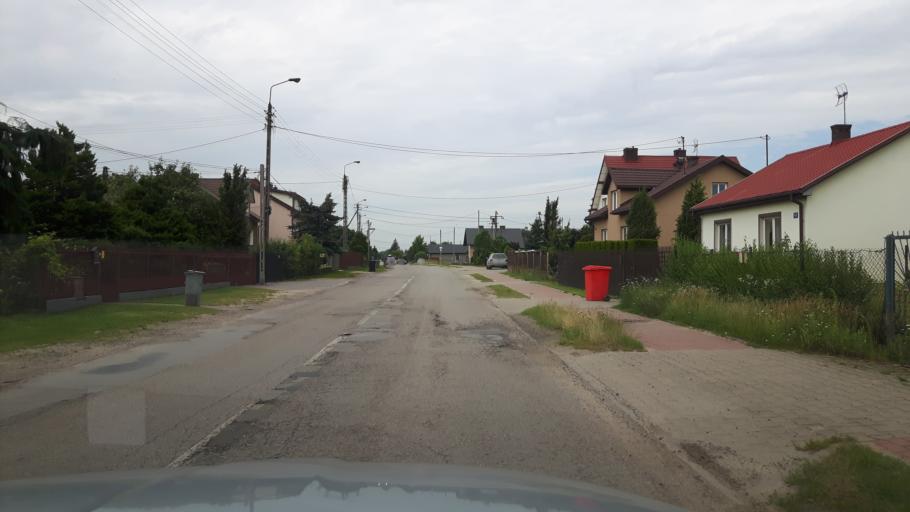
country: PL
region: Masovian Voivodeship
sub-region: Powiat wolominski
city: Kobylka
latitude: 52.3121
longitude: 21.2112
